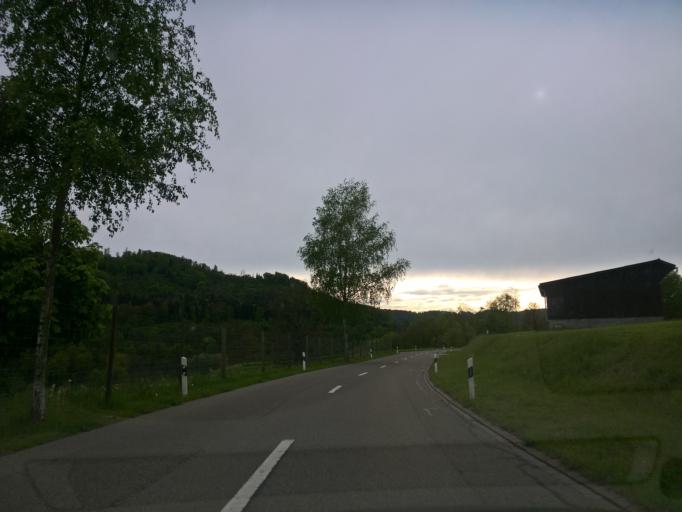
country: CH
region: Zurich
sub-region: Bezirk Winterthur
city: Pfungen
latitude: 47.5230
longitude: 8.6242
